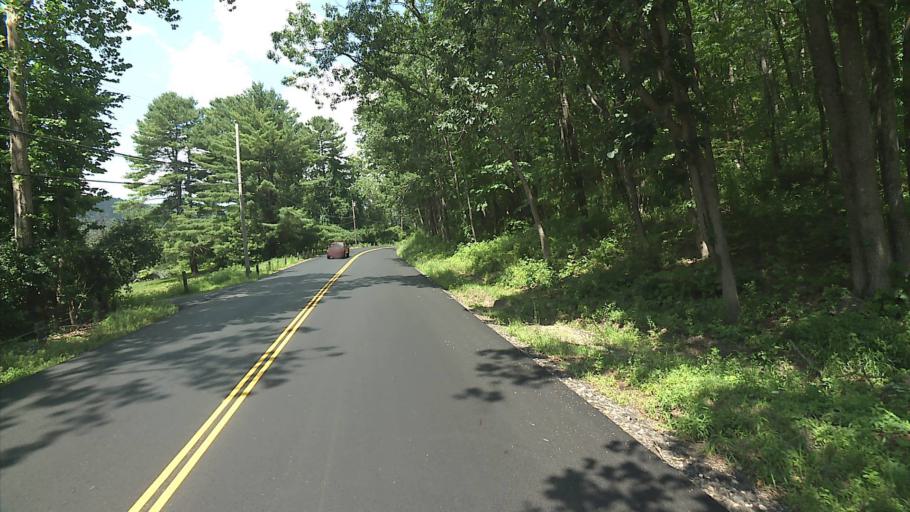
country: US
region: Connecticut
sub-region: Litchfield County
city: Canaan
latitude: 41.9766
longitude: -73.3585
